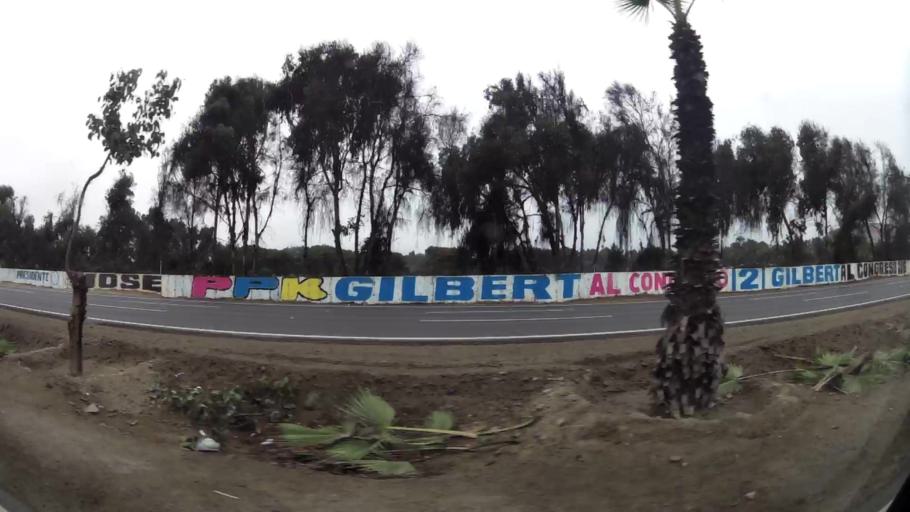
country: PE
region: Lima
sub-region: Lima
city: Punta Hermosa
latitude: -12.2633
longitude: -76.9102
